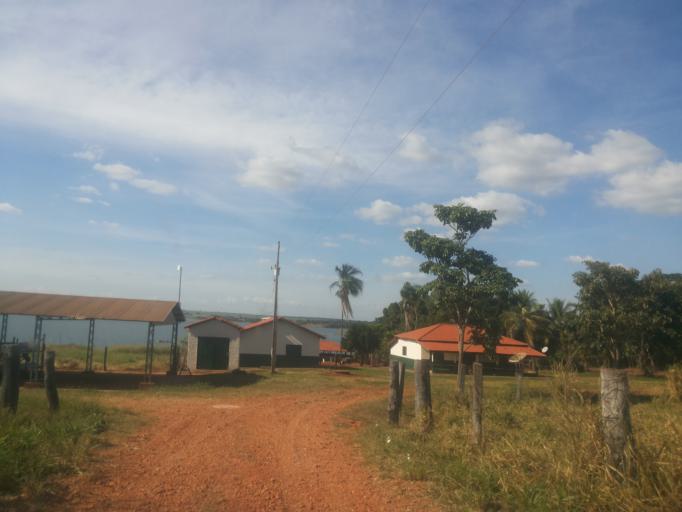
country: BR
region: Minas Gerais
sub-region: Santa Vitoria
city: Santa Vitoria
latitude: -19.0031
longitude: -50.3962
